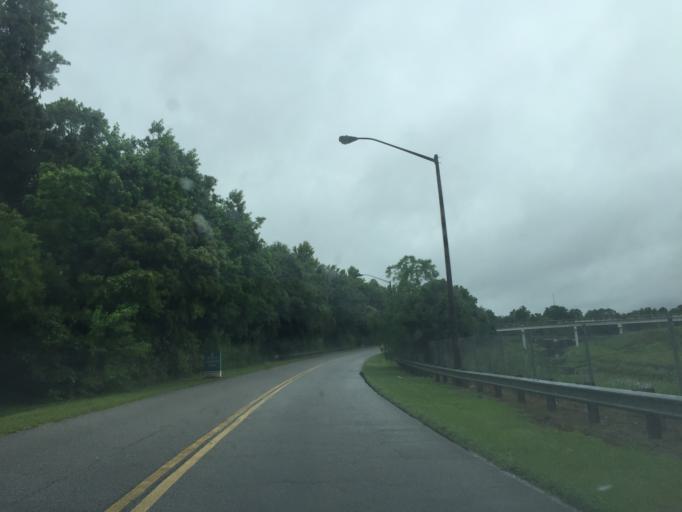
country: US
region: Georgia
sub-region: Chatham County
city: Thunderbolt
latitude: 32.0324
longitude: -81.0854
